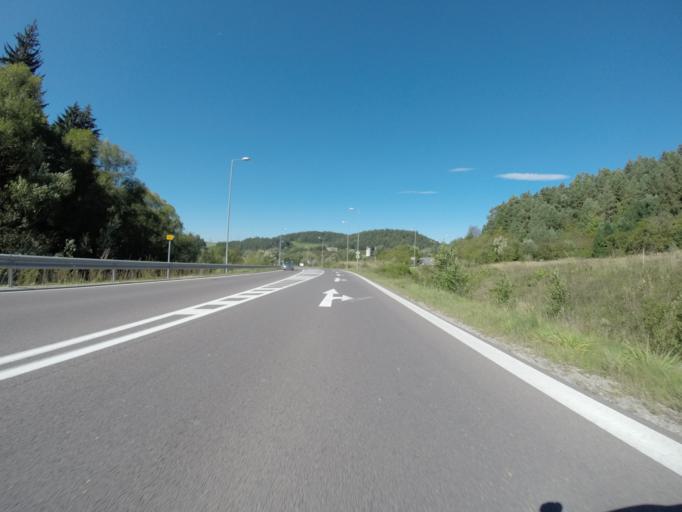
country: SK
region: Trenciansky
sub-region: Okres Povazska Bystrica
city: Povazska Bystrica
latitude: 49.1000
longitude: 18.4440
